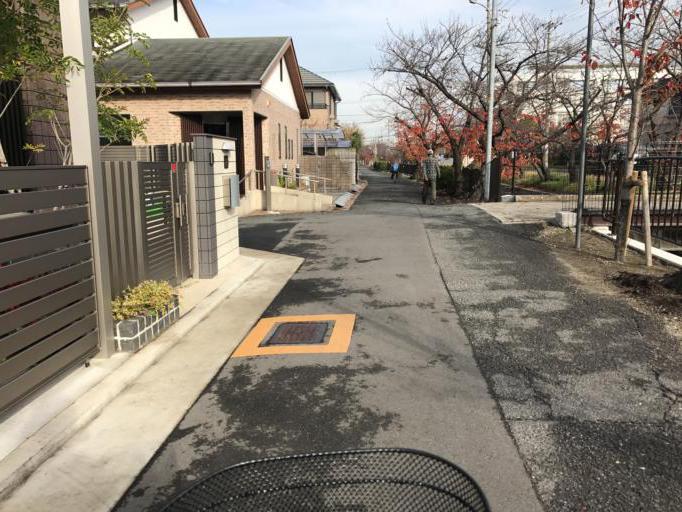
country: JP
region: Osaka
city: Yao
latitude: 34.6151
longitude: 135.6230
